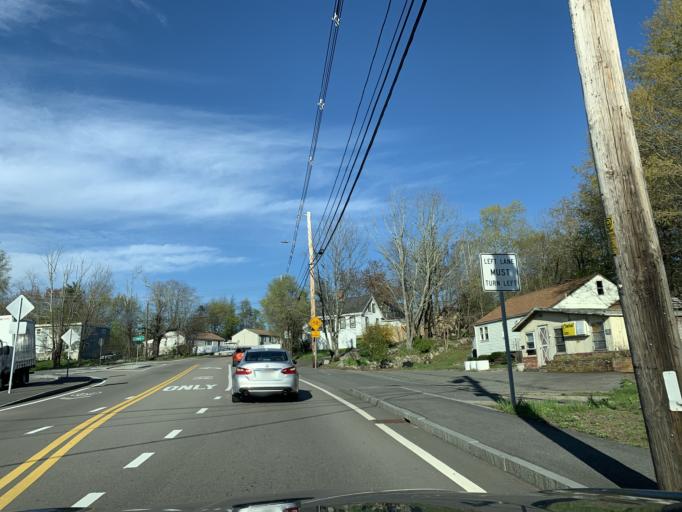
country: US
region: Massachusetts
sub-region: Norfolk County
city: Stoughton
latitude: 42.1308
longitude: -71.1284
